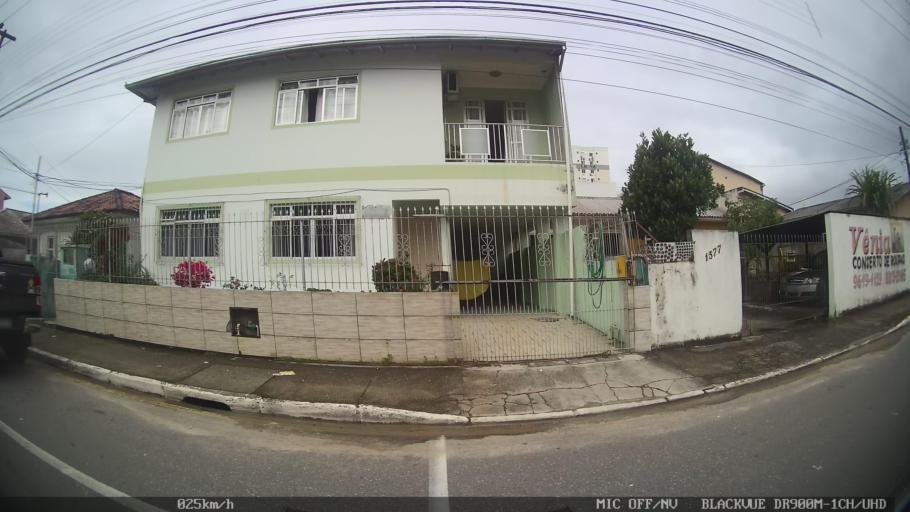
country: BR
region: Santa Catarina
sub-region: Sao Jose
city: Campinas
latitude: -27.5590
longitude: -48.6295
